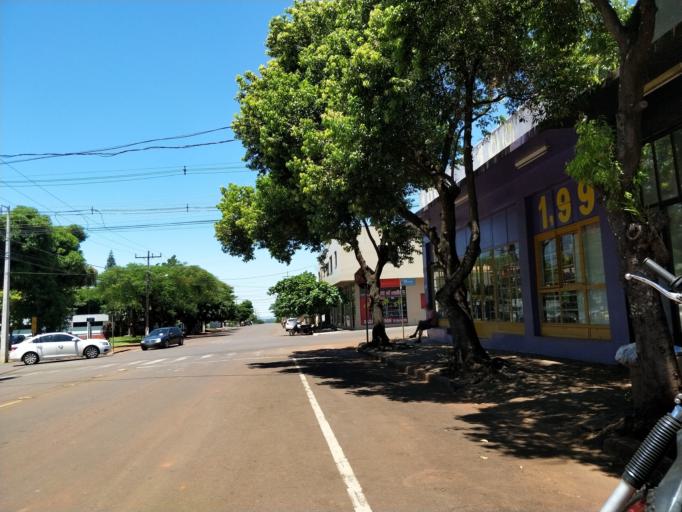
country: BR
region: Parana
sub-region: Marechal Candido Rondon
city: Marechal Candido Rondon
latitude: -24.5653
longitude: -54.0584
